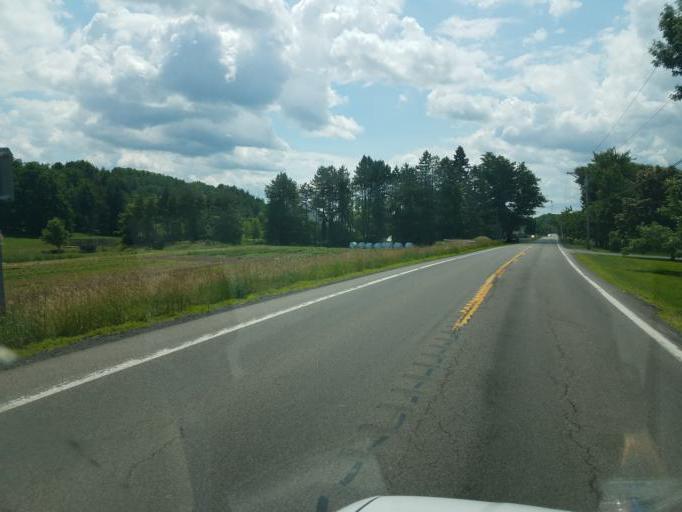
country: US
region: New York
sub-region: Wayne County
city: Clyde
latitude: 43.0987
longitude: -76.8679
